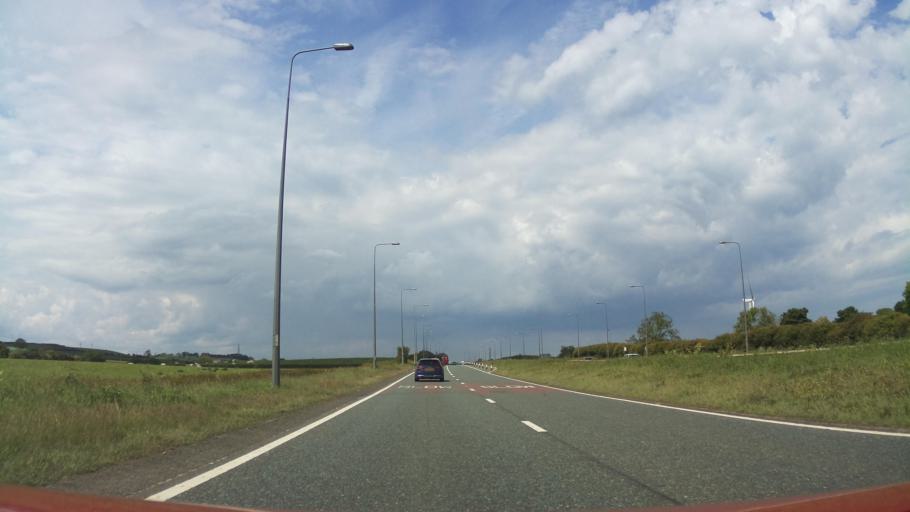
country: GB
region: England
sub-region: Hartlepool
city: Elwick
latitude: 54.6856
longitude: -1.3038
